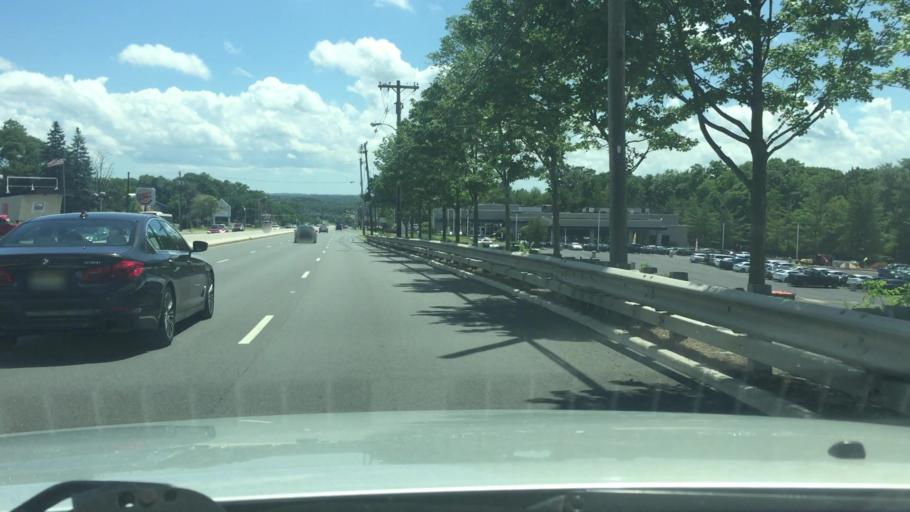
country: US
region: New Jersey
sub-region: Middlesex County
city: Old Bridge
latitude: 40.4186
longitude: -74.3742
